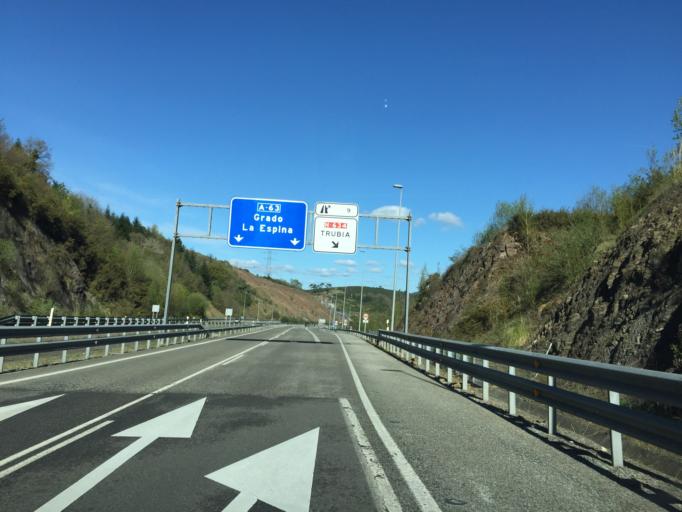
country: ES
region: Asturias
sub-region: Province of Asturias
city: Castandiello
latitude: 43.3595
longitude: -5.9448
